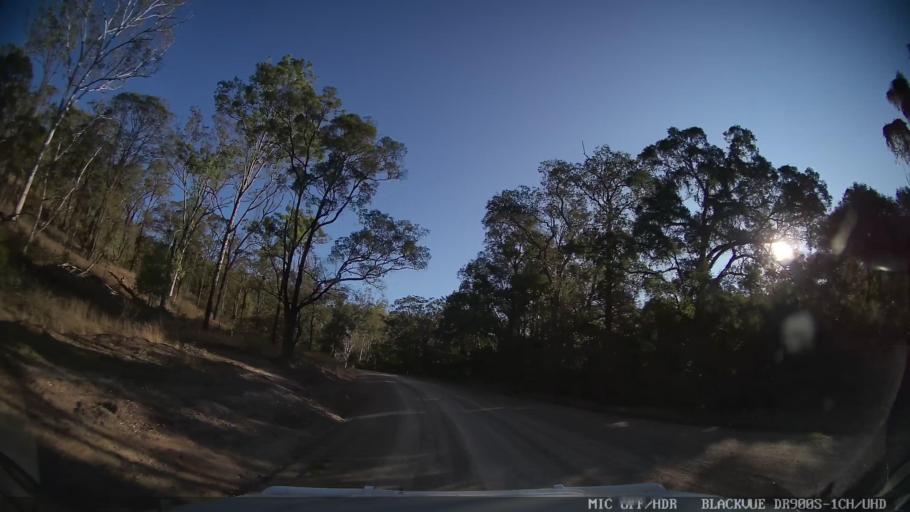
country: AU
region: Queensland
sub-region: Gladstone
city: Toolooa
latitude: -24.6952
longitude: 151.4056
